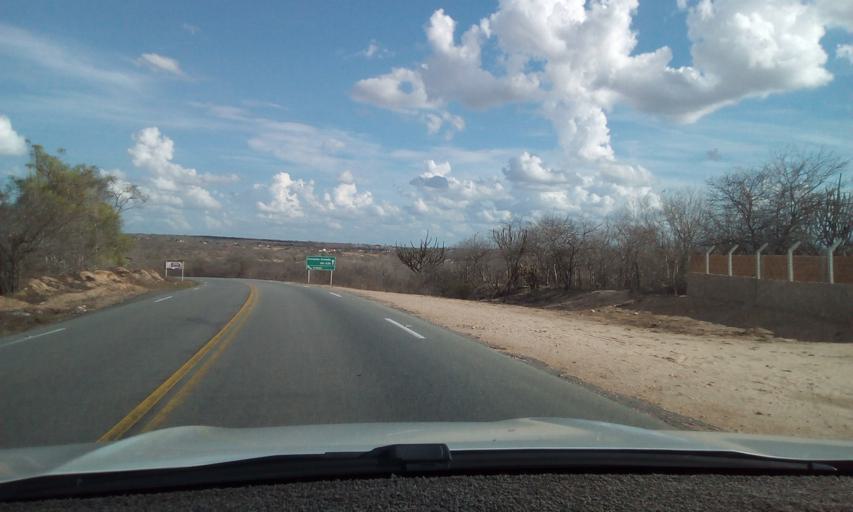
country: BR
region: Paraiba
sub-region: Soledade
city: Soledade
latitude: -6.8946
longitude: -36.3965
